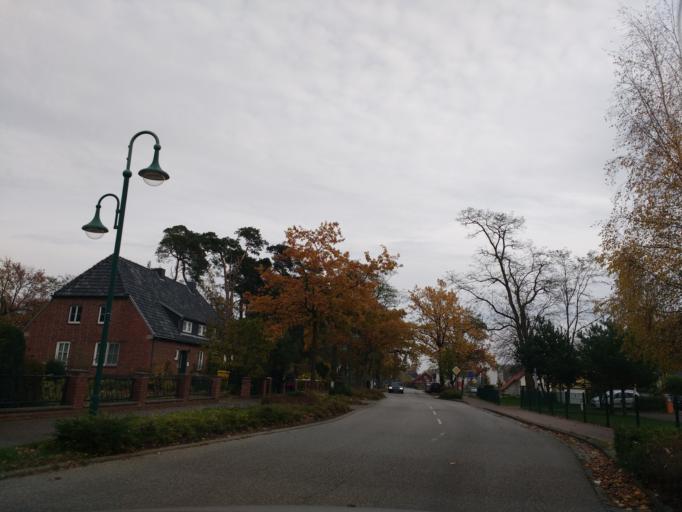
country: DE
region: Mecklenburg-Vorpommern
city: Ostseebad Boltenhagen
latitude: 53.9798
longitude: 11.2335
